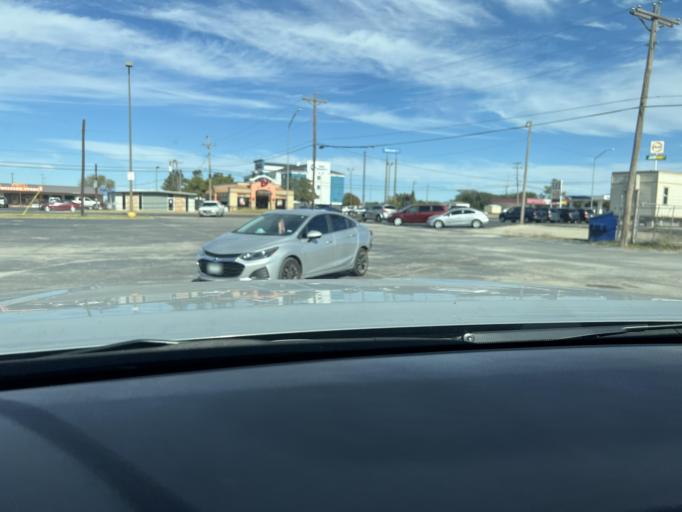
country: US
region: Texas
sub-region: Eastland County
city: Eastland
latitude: 32.4010
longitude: -98.7936
